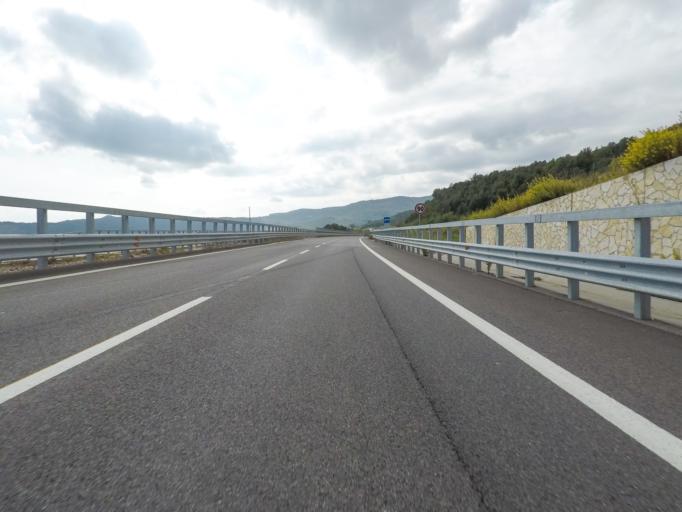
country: IT
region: Tuscany
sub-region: Provincia di Grosseto
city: Civitella Marittima
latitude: 43.0941
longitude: 11.2990
